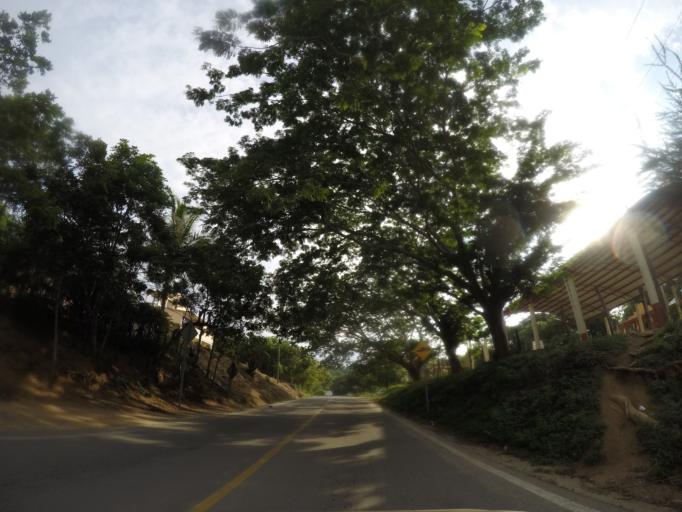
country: MX
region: Oaxaca
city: San Pedro Pochutla
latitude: 15.7154
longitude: -96.4791
